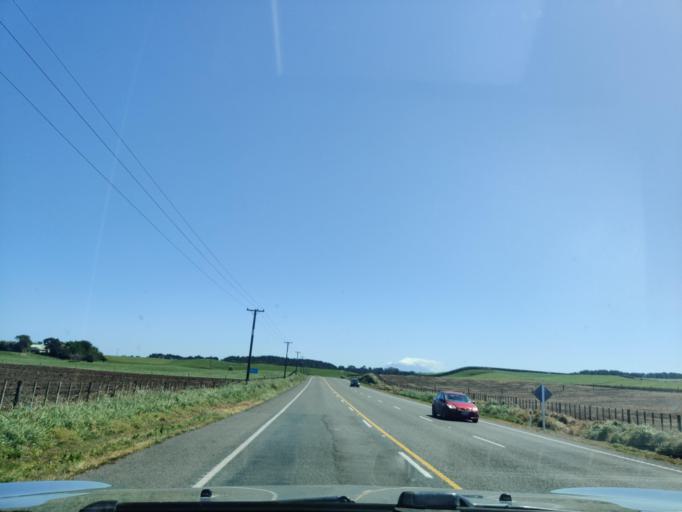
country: NZ
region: Taranaki
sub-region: South Taranaki District
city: Patea
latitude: -39.6929
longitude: 174.4261
